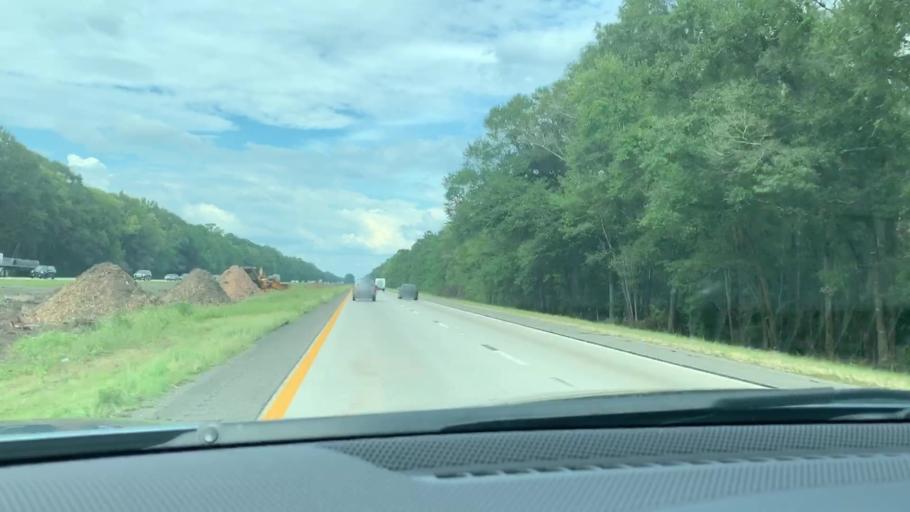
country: US
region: South Carolina
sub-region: Jasper County
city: Hardeeville
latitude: 32.3568
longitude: -81.0400
